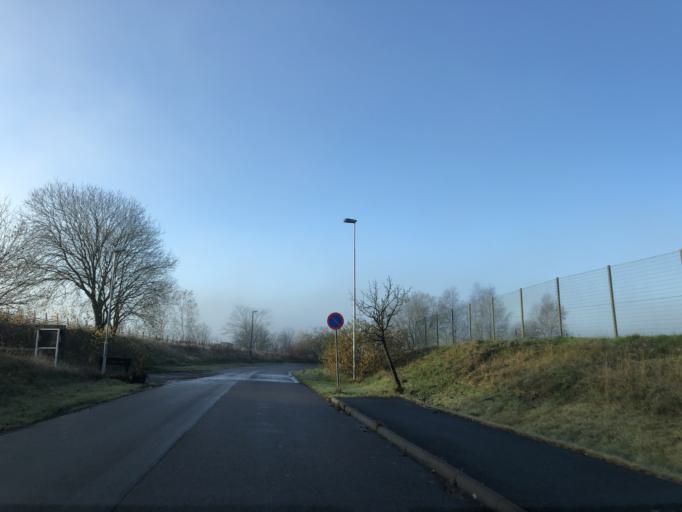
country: SE
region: Vaestra Goetaland
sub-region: Goteborg
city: Rannebergen
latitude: 57.7930
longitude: 12.0542
